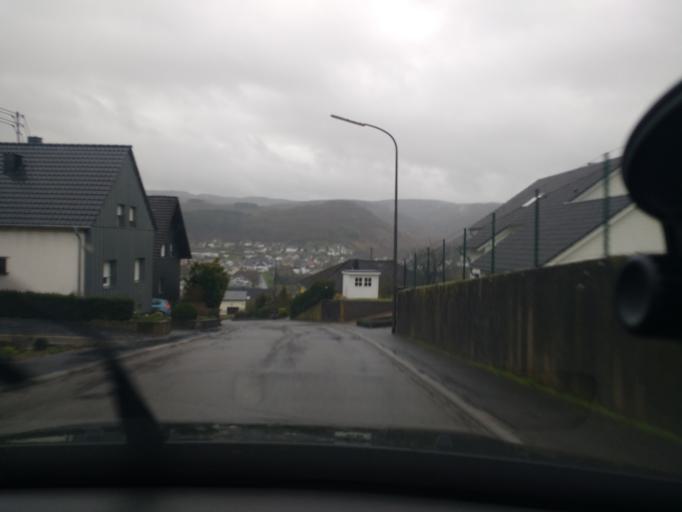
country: DE
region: Rheinland-Pfalz
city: Wiltingen
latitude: 49.6654
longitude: 6.6242
